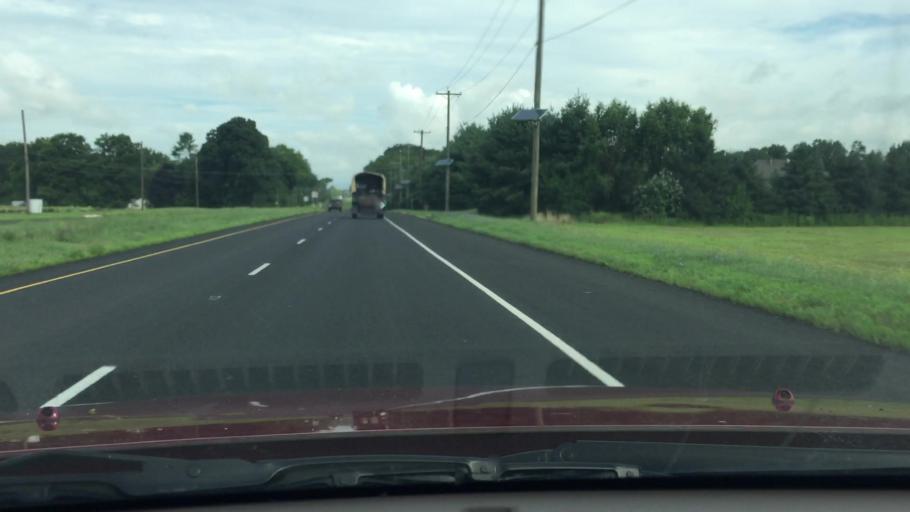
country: US
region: New Jersey
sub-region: Burlington County
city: Bordentown
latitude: 40.0976
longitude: -74.6860
